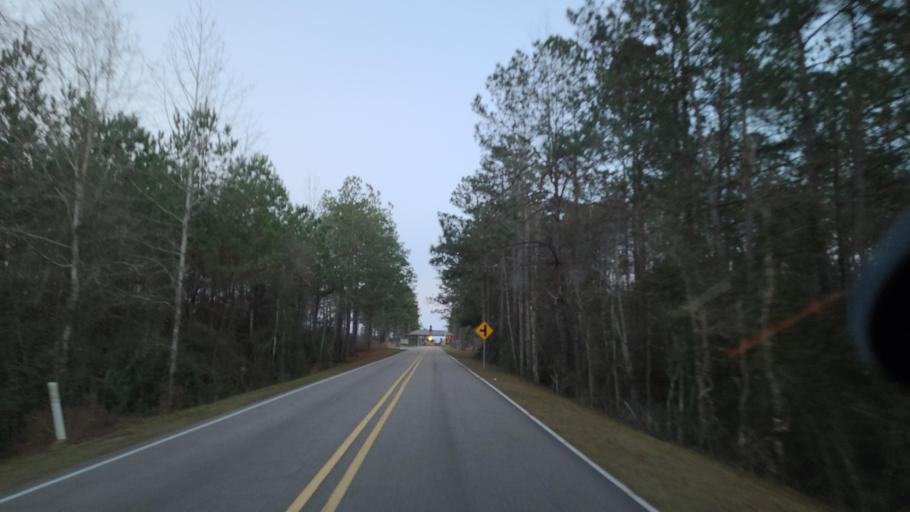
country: US
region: Mississippi
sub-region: Forrest County
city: Hattiesburg
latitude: 31.2098
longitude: -89.2463
